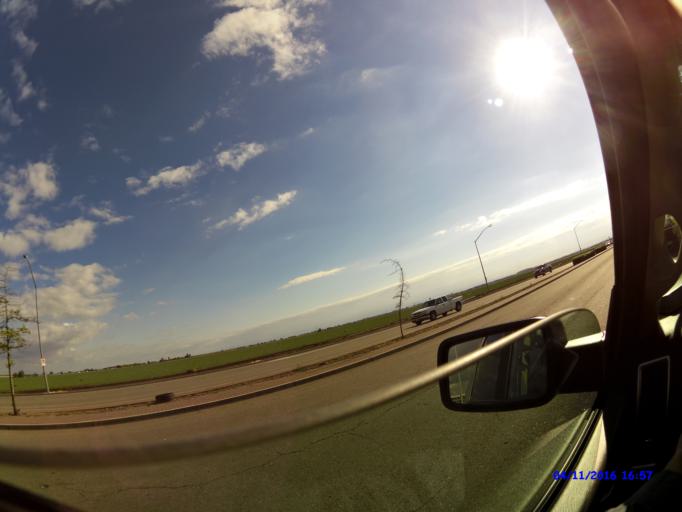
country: US
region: California
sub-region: San Joaquin County
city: Kennedy
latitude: 37.9044
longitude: -121.2254
